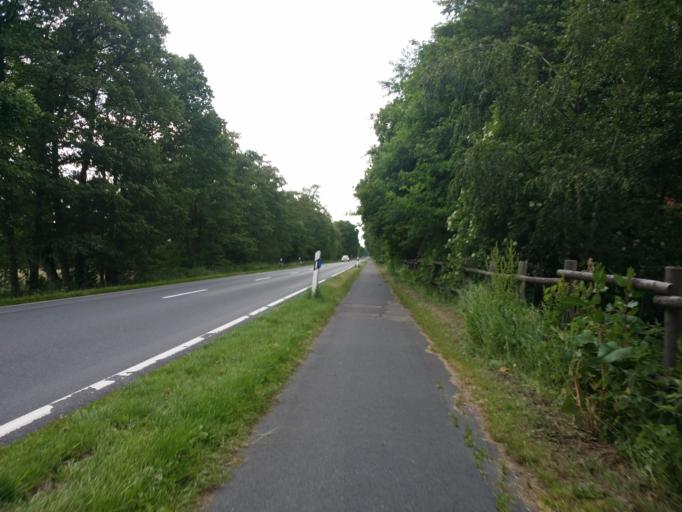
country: DE
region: Lower Saxony
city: Friedeburg
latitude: 53.4974
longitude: 7.8245
